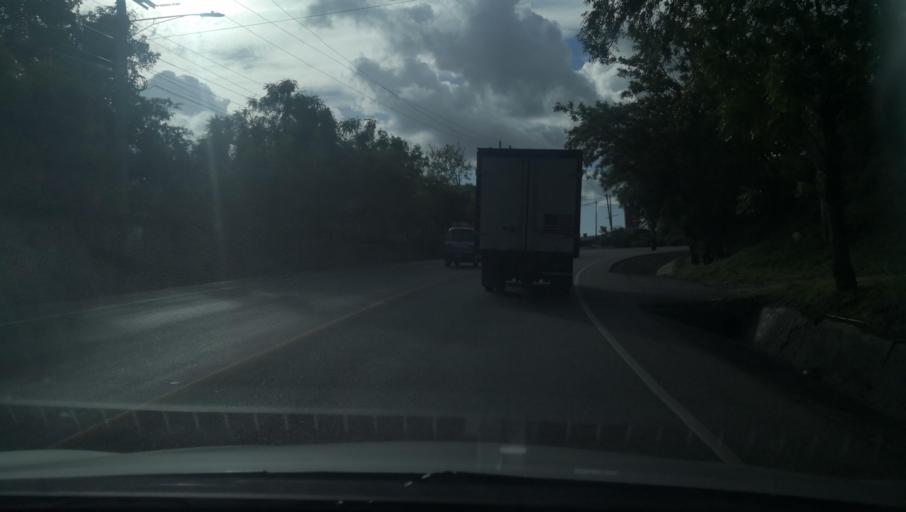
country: NI
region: Nueva Segovia
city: Ocotal
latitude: 13.6136
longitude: -86.4732
